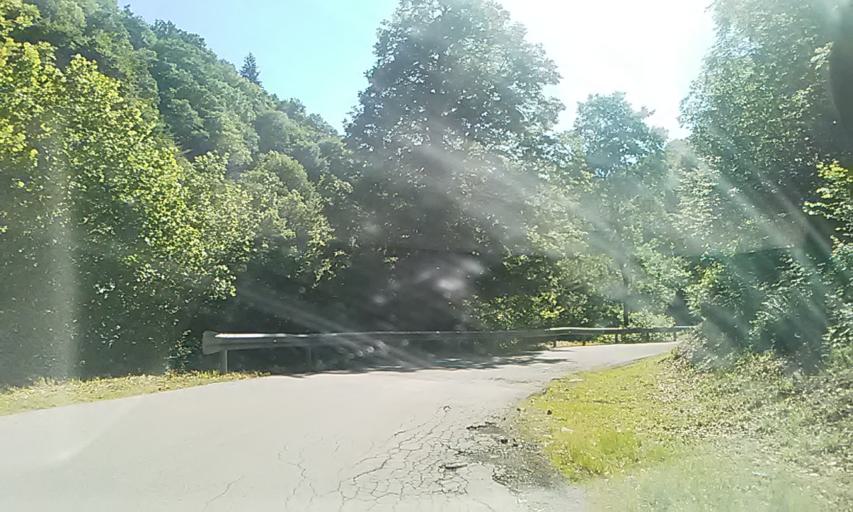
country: IT
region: Piedmont
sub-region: Provincia di Vercelli
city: Civiasco
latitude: 45.8426
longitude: 8.2822
